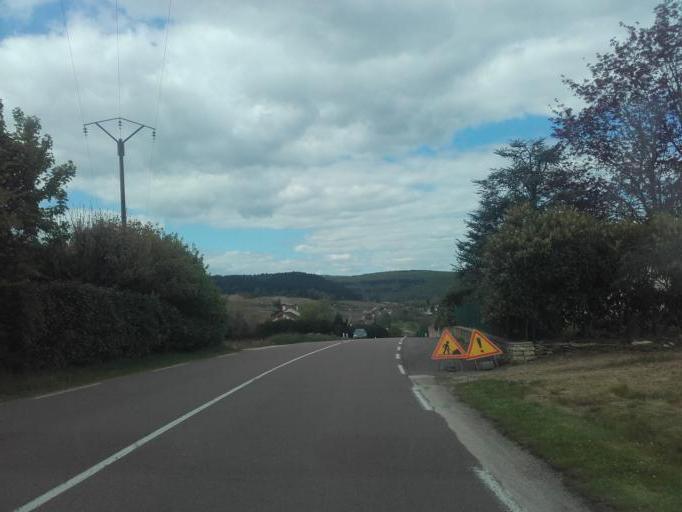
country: FR
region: Bourgogne
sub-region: Departement de la Cote-d'Or
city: Meursault
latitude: 46.9890
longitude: 4.7699
